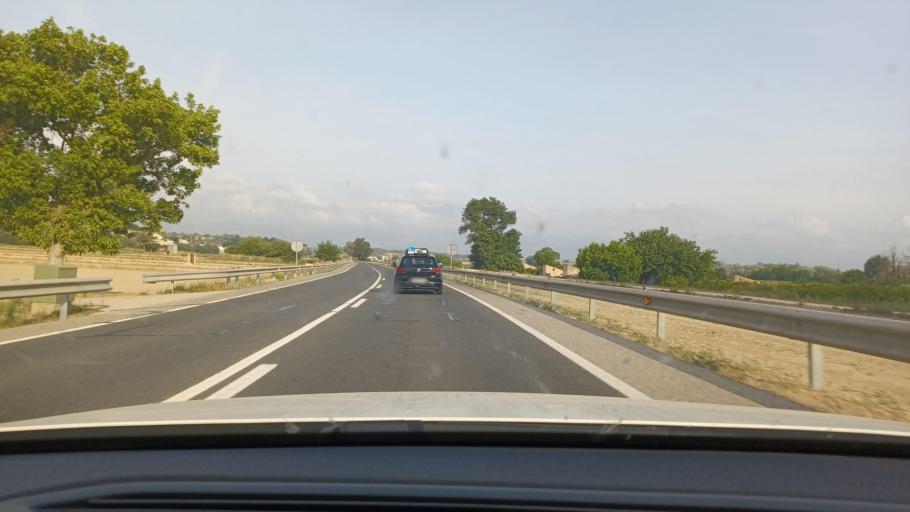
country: ES
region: Catalonia
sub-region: Provincia de Tarragona
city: Tortosa
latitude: 40.7751
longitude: 0.5245
